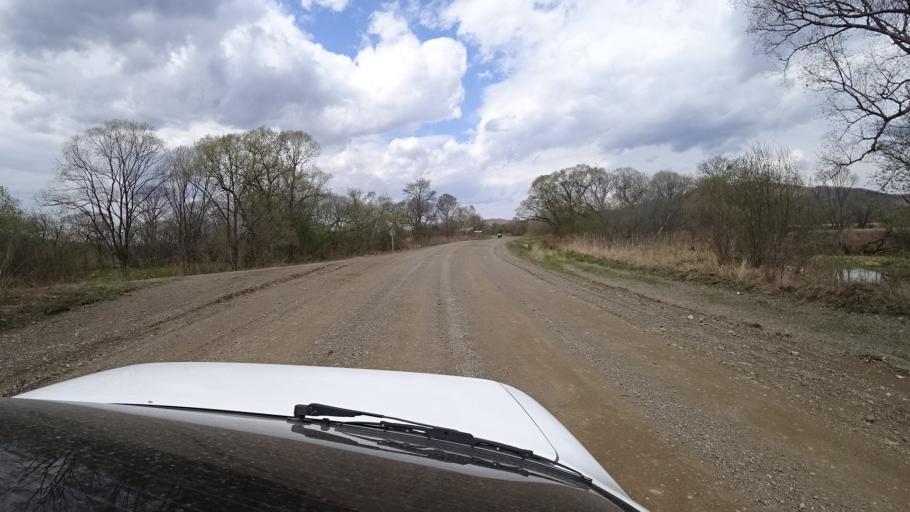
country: RU
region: Primorskiy
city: Novopokrovka
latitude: 45.6115
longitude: 134.2746
